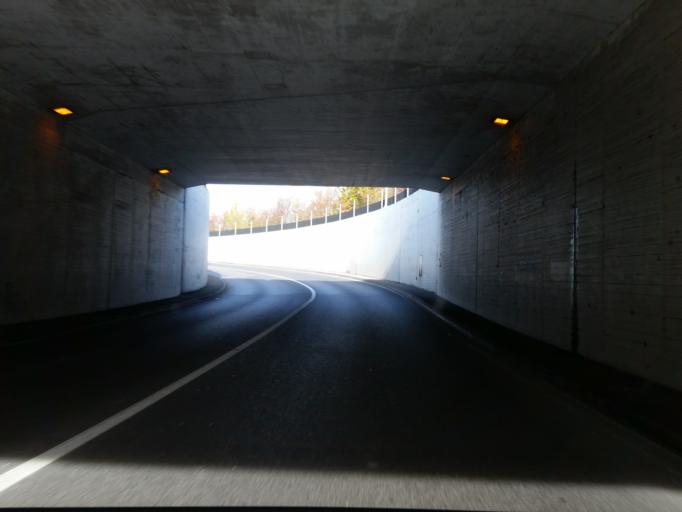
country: DE
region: Baden-Wuerttemberg
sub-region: Freiburg Region
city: Konstanz
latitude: 47.6535
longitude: 9.1653
